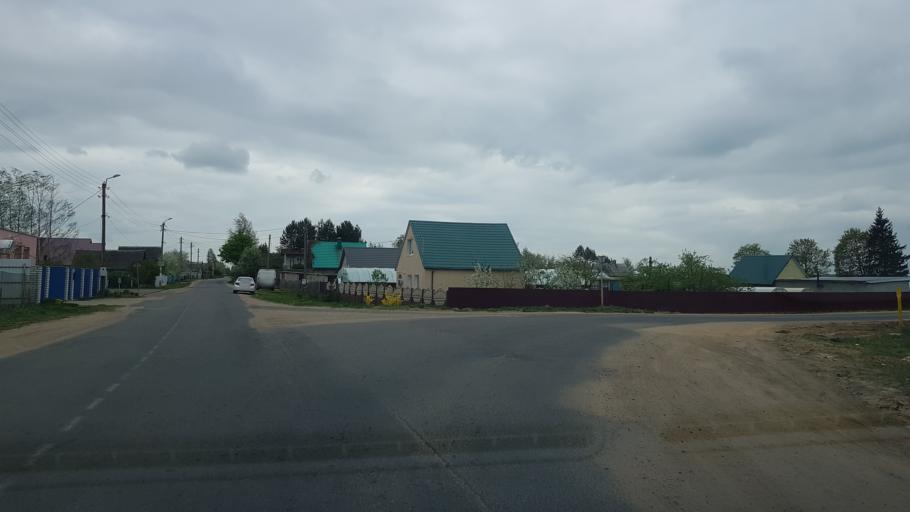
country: BY
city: Fanipol
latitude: 53.7214
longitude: 27.3143
